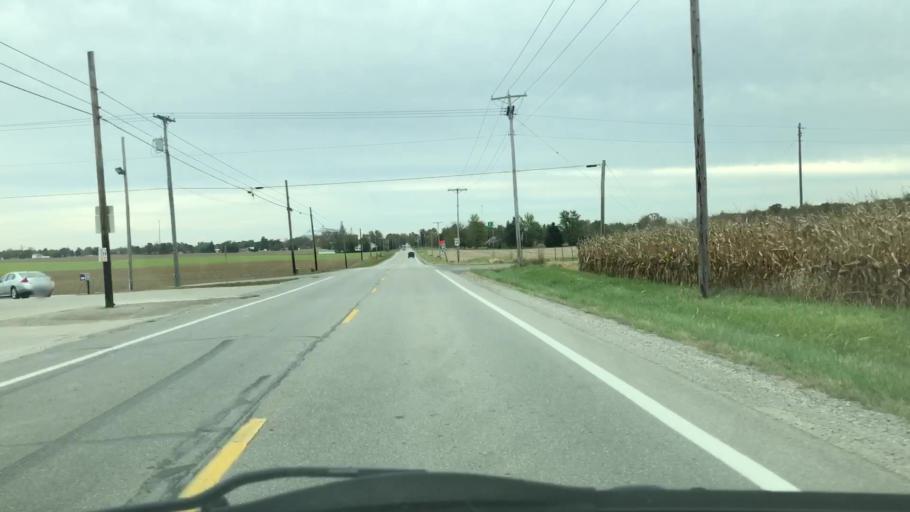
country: US
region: Ohio
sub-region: Williams County
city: Edgerton
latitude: 41.5714
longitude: -84.7692
